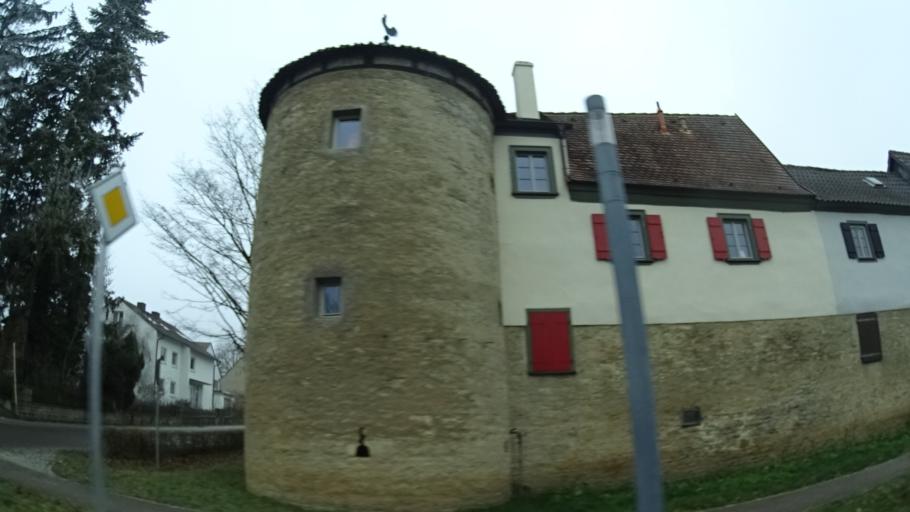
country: DE
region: Bavaria
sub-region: Regierungsbezirk Unterfranken
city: Sulzfeld am Main
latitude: 49.7064
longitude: 10.1328
